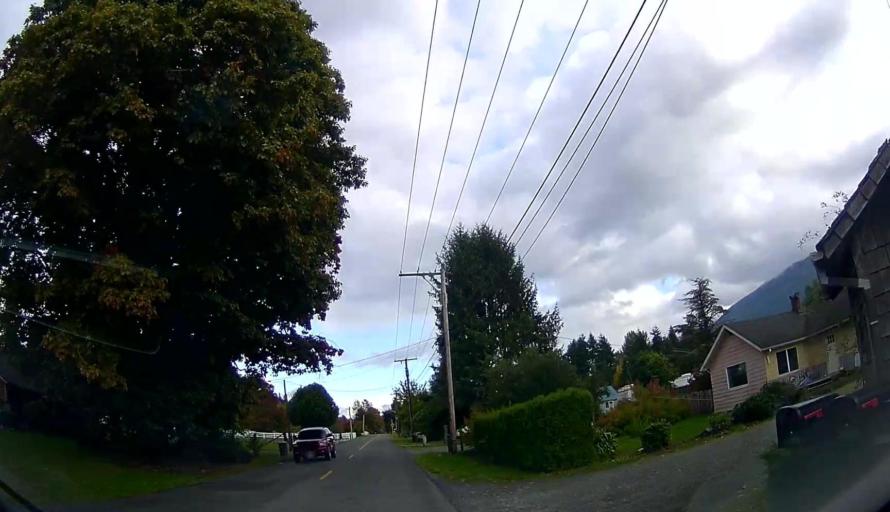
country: US
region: Washington
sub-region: Skagit County
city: Sedro-Woolley
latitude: 48.5336
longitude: -122.0028
